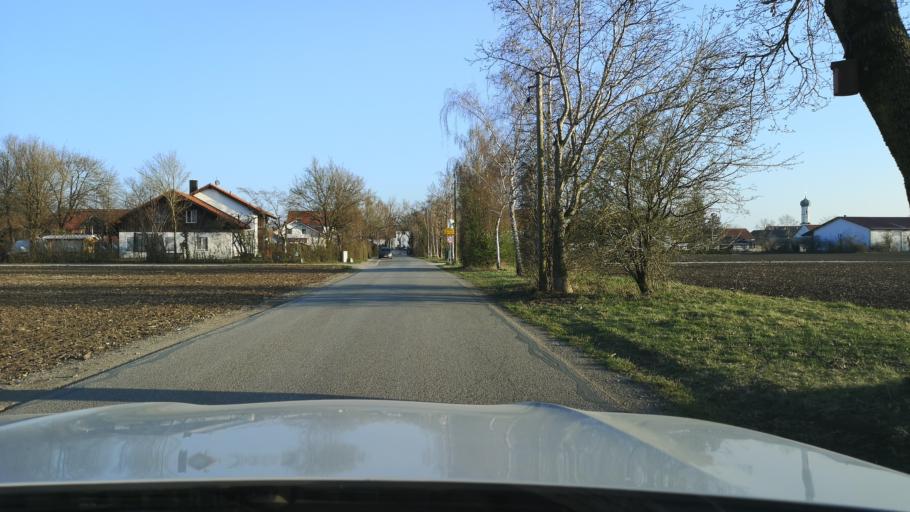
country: DE
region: Bavaria
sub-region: Upper Bavaria
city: Kirchheim bei Muenchen
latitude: 48.1814
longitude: 11.7552
